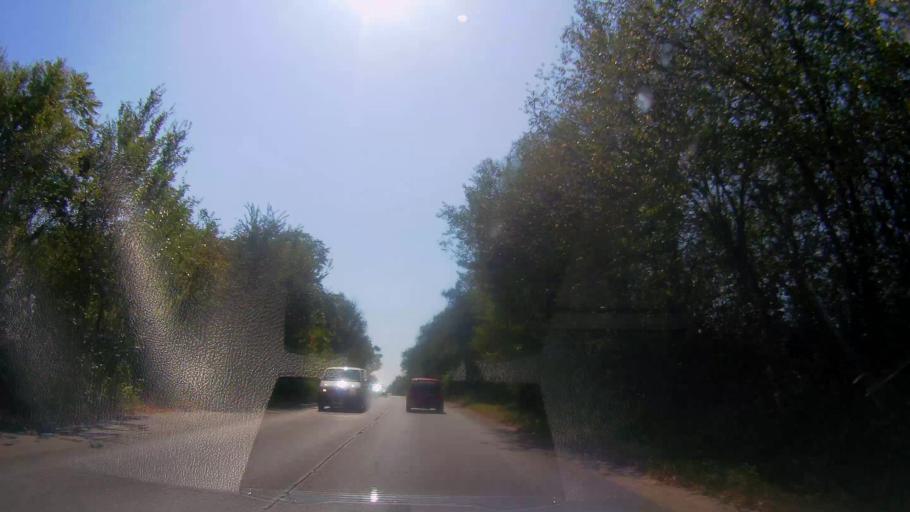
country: BG
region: Veliko Turnovo
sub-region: Obshtina Gorna Oryakhovitsa
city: Purvomaytsi
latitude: 43.2559
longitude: 25.6424
